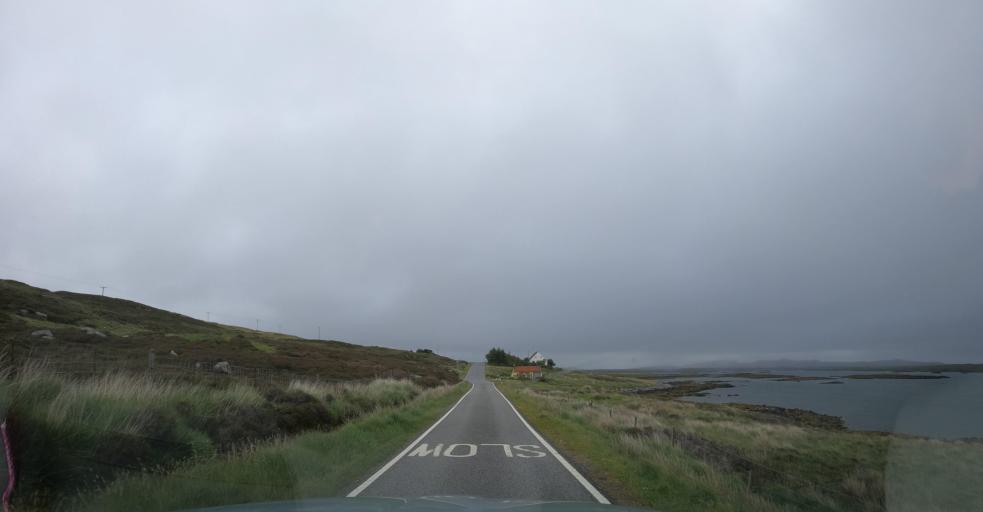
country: GB
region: Scotland
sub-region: Eilean Siar
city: Isle of North Uist
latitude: 57.6237
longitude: -7.2019
